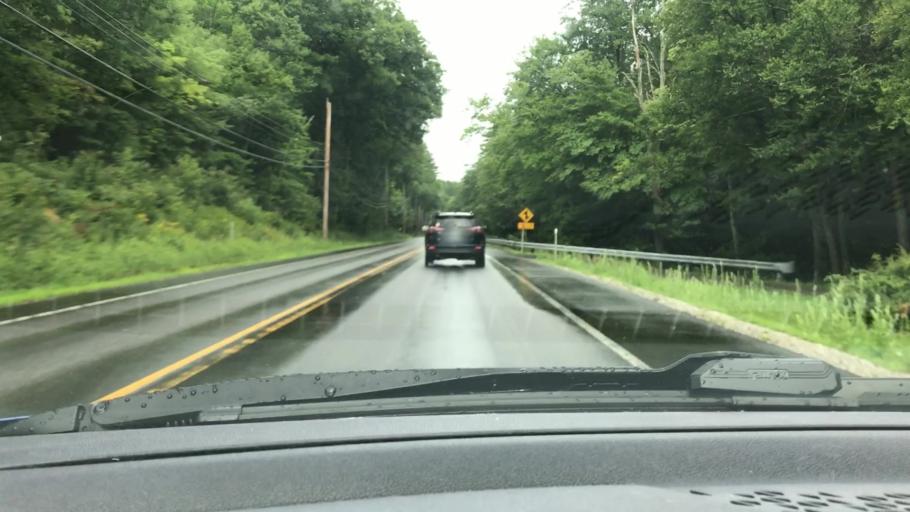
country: US
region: New Hampshire
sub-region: Merrimack County
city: Epsom
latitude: 43.2233
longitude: -71.3187
